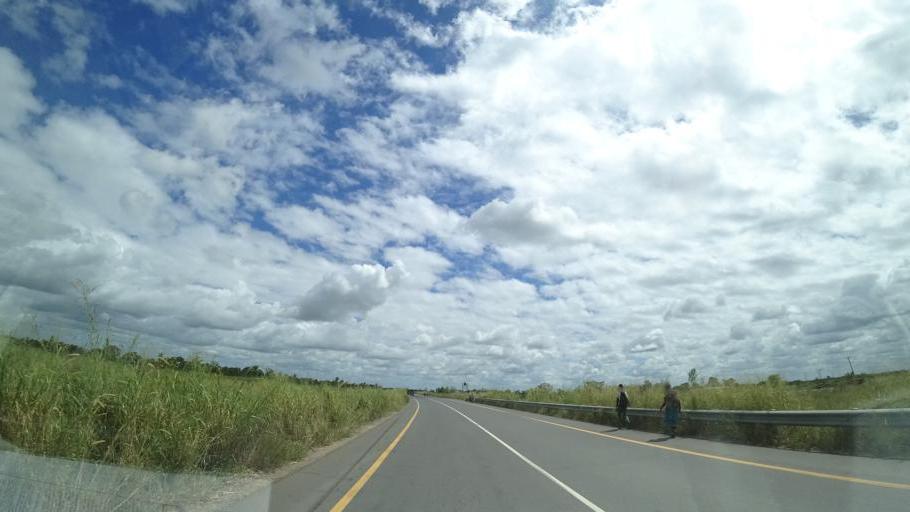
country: MZ
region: Sofala
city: Dondo
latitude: -19.3975
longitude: 34.4267
